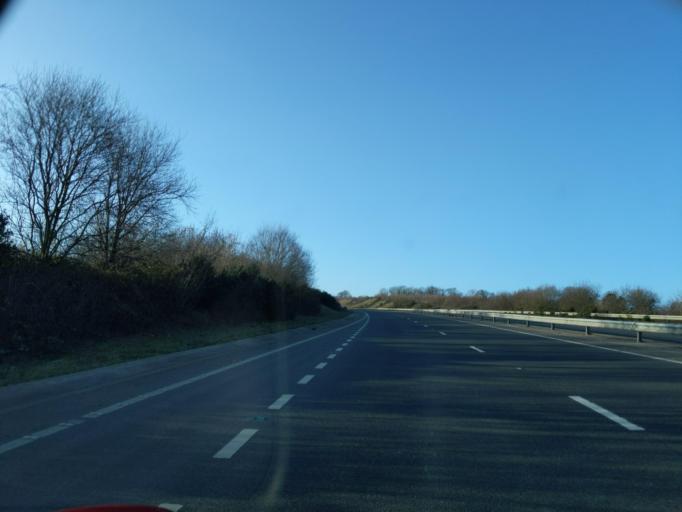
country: GB
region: England
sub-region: Cornwall
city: Liskeard
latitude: 50.4592
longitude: -4.5101
